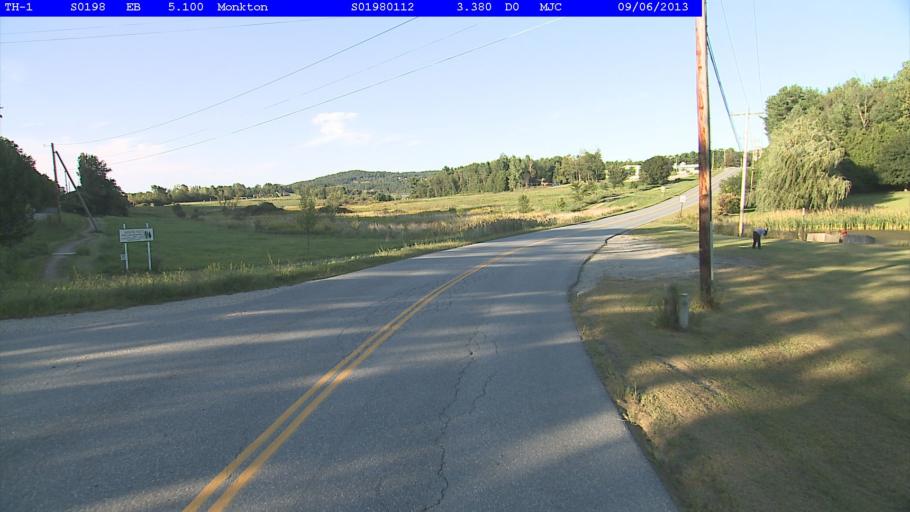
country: US
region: Vermont
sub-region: Chittenden County
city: Hinesburg
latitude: 44.2420
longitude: -73.1424
